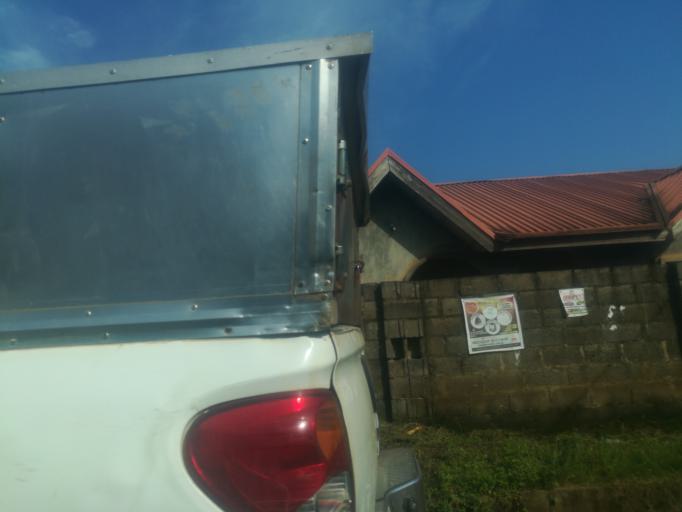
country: NG
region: Oyo
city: Ibadan
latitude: 7.3530
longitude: 3.8249
